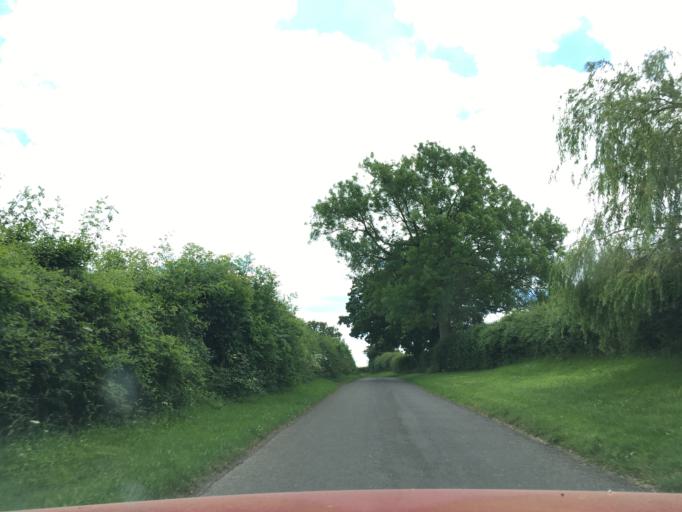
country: GB
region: England
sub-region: Hampshire
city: Highclere
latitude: 51.2737
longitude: -1.4208
